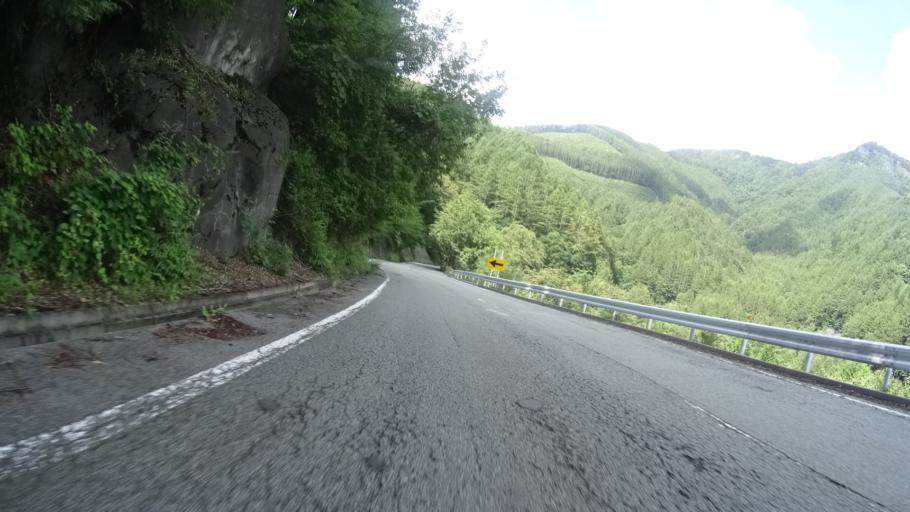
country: JP
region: Yamanashi
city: Enzan
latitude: 35.8017
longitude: 138.6694
